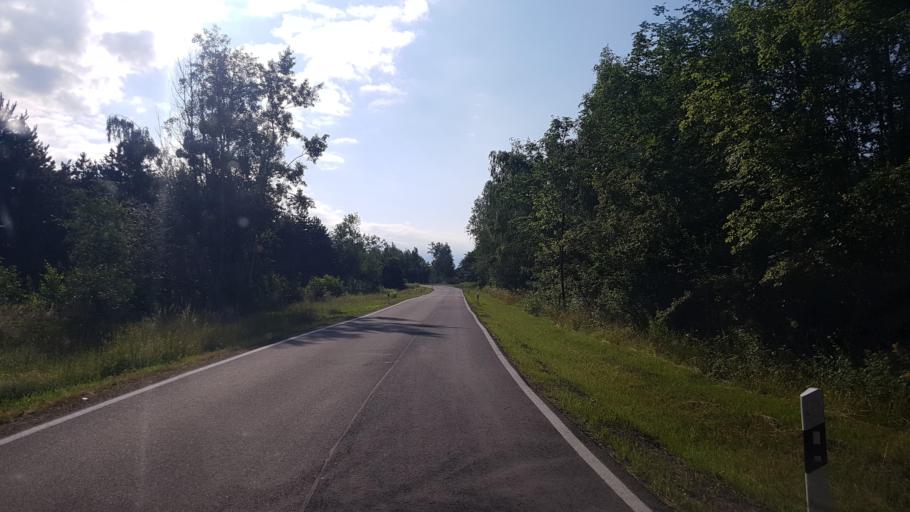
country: DE
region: Brandenburg
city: Grossraschen
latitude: 51.5783
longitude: 14.0159
